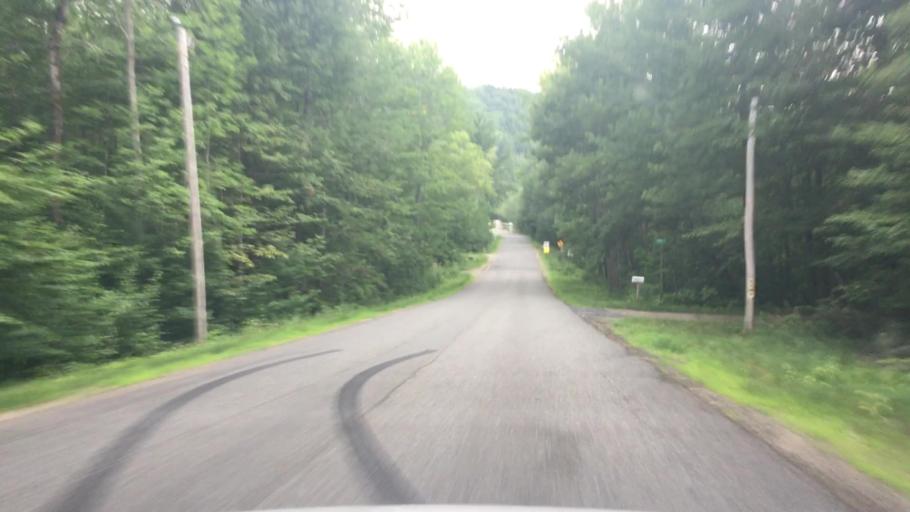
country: US
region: Maine
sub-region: Knox County
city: Washington
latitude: 44.3724
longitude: -69.3483
